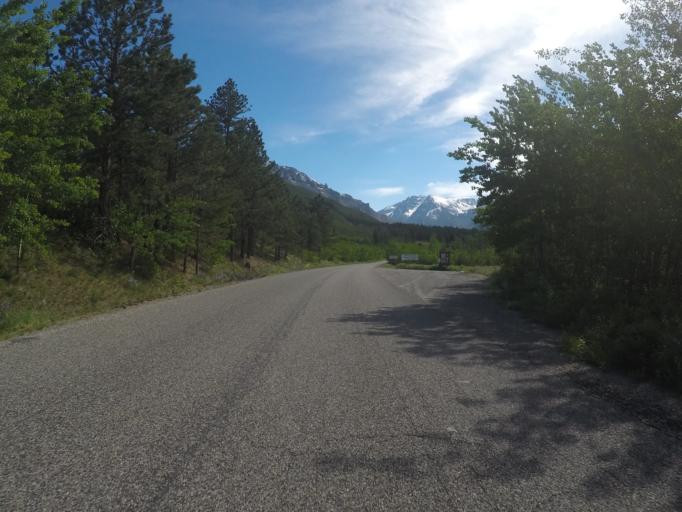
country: US
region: Montana
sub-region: Stillwater County
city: Absarokee
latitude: 45.2494
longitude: -109.5741
